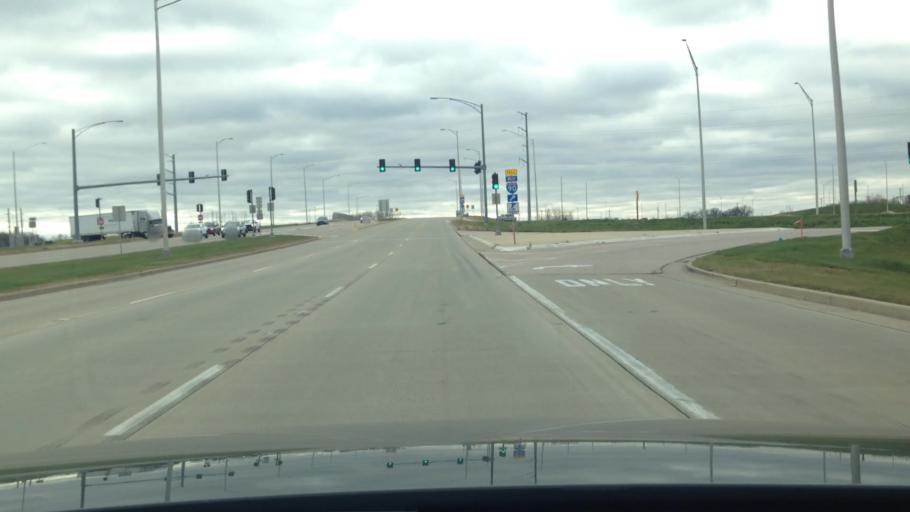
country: US
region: Illinois
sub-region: McHenry County
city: Huntley
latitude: 42.1255
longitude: -88.4330
